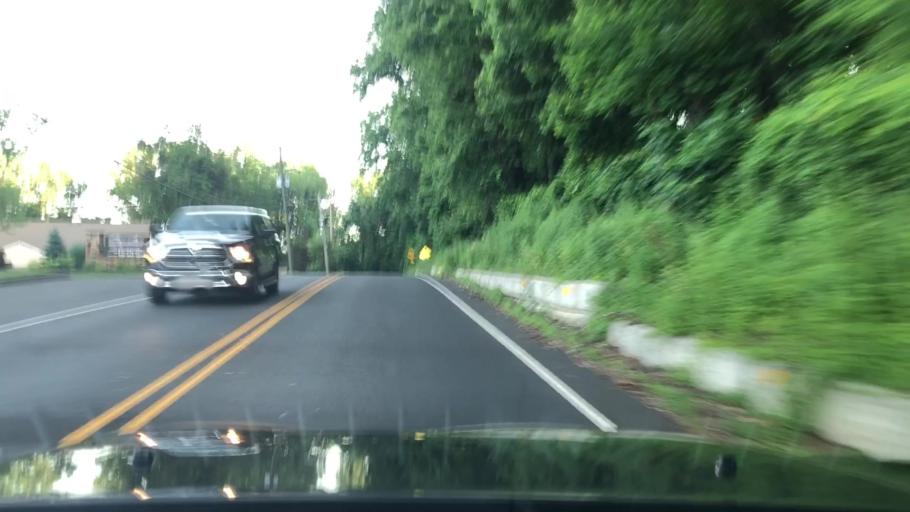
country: US
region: Pennsylvania
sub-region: Bucks County
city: Langhorne Manor
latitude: 40.1723
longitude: -74.9015
